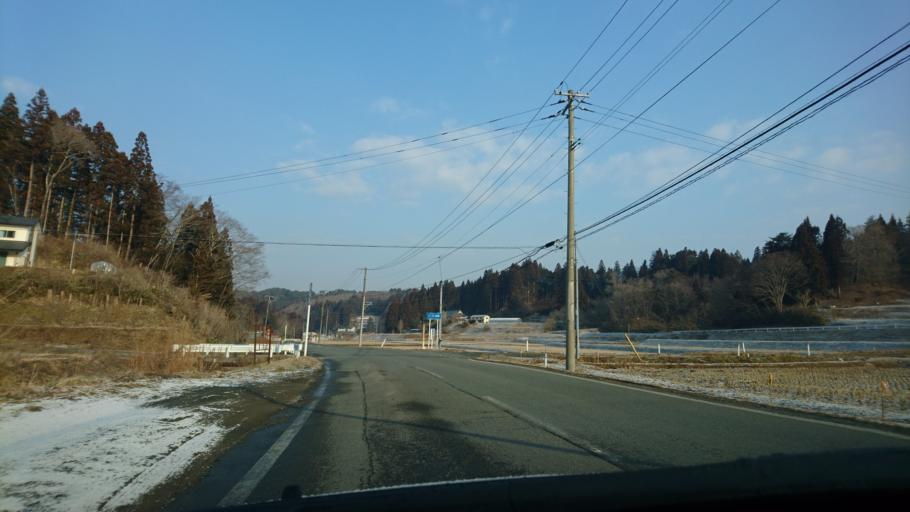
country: JP
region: Iwate
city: Ichinoseki
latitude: 38.9278
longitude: 141.3861
